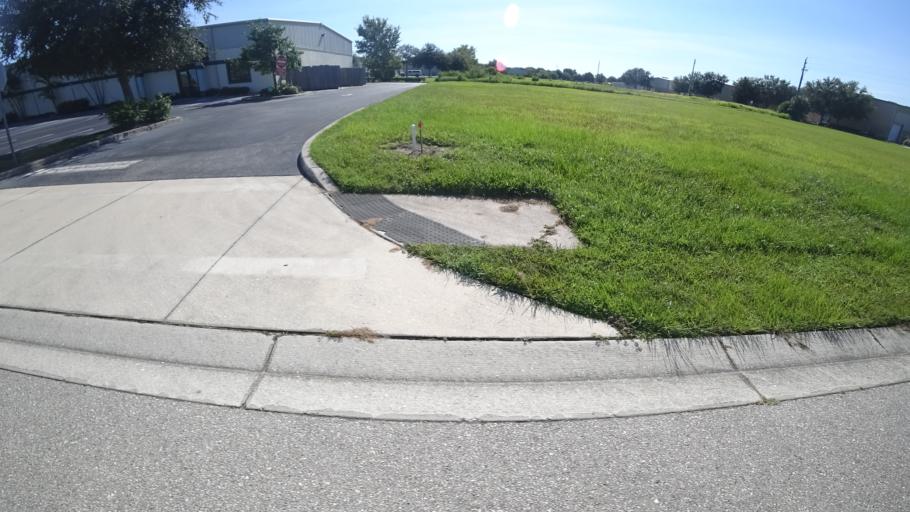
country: US
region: Florida
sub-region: Manatee County
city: Whitfield
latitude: 27.4120
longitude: -82.5372
